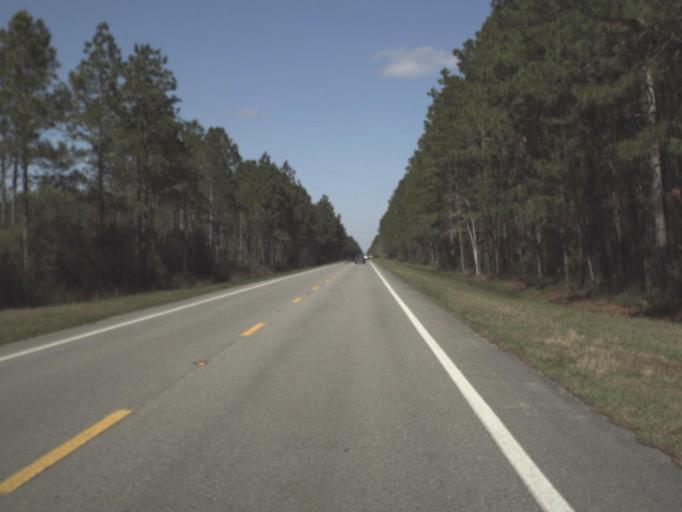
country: US
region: Florida
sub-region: Gulf County
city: Port Saint Joe
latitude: 29.9315
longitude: -85.1927
